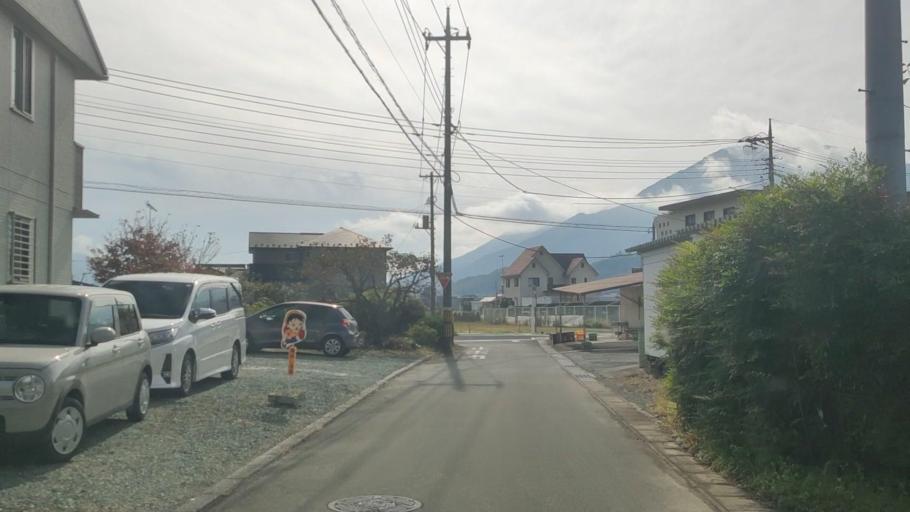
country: JP
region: Yamanashi
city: Ryuo
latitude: 35.4403
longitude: 138.4446
